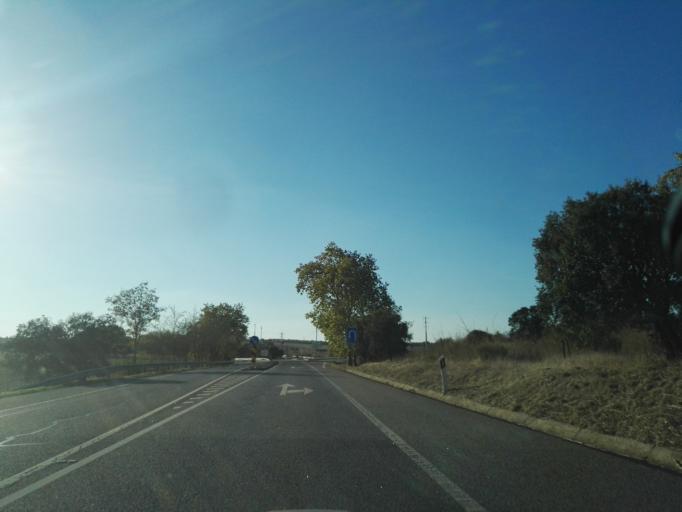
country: PT
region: Evora
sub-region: Vila Vicosa
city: Vila Vicosa
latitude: 38.8541
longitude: -7.3278
